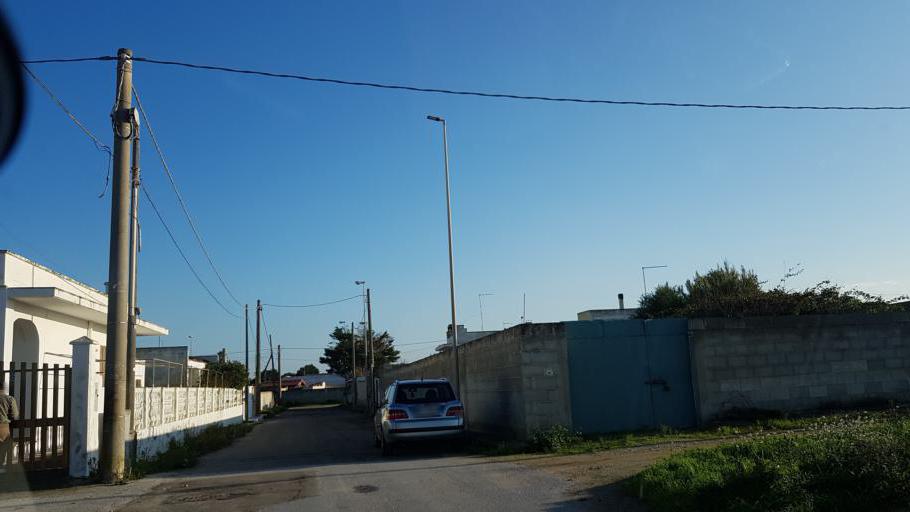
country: IT
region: Apulia
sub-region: Provincia di Brindisi
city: Torchiarolo
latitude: 40.5148
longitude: 18.0949
